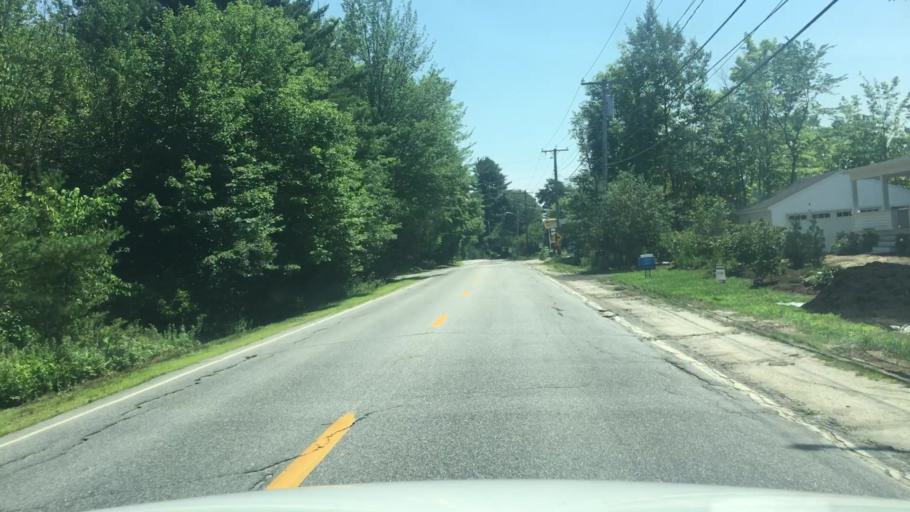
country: US
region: Maine
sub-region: Cumberland County
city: Cumberland Center
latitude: 43.7824
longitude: -70.2576
